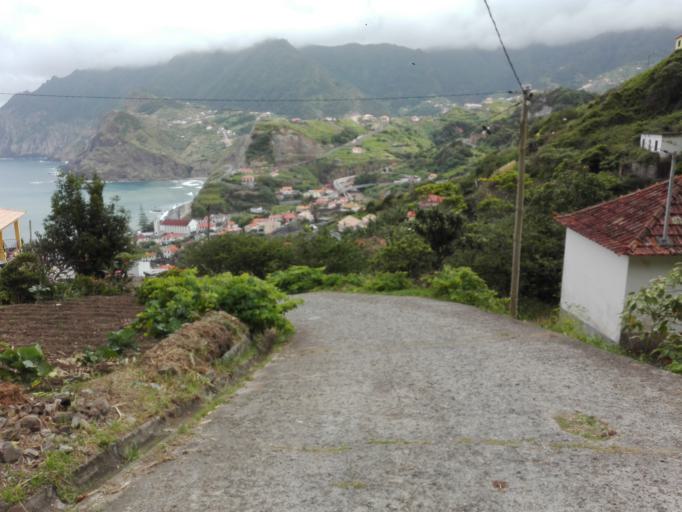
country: PT
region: Madeira
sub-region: Santana
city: Santana
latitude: 32.7747
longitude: -16.8335
